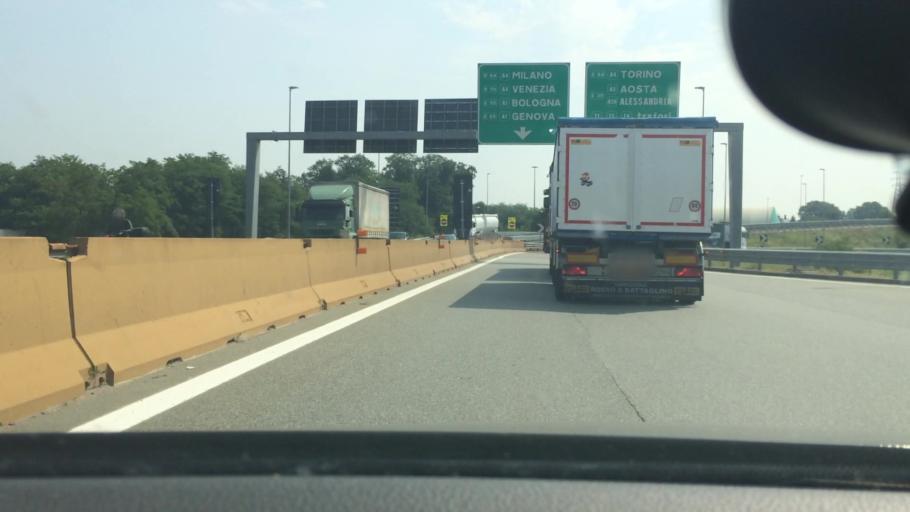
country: IT
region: Lombardy
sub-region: Citta metropolitana di Milano
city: Arluno
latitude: 45.5012
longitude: 8.9254
